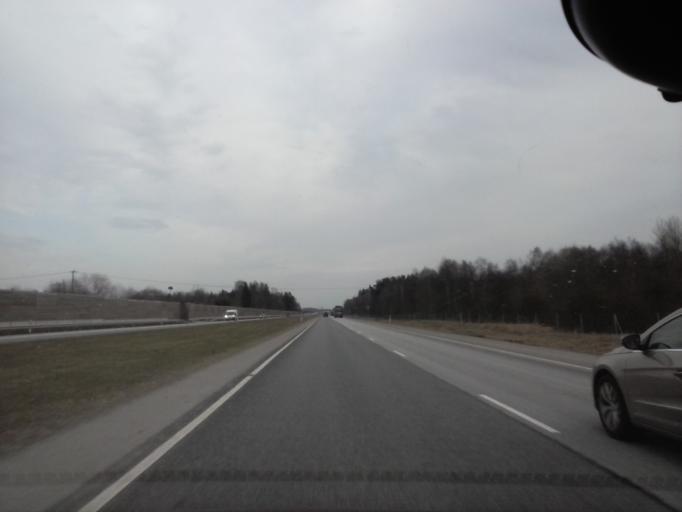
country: EE
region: Harju
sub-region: Rae vald
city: Jueri
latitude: 59.3255
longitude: 24.9196
